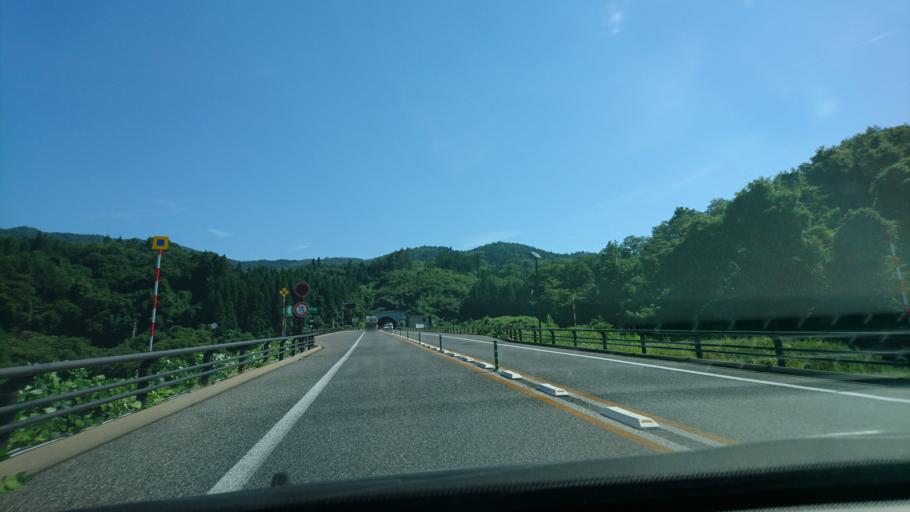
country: JP
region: Iwate
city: Kitakami
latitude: 39.2923
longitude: 141.2893
